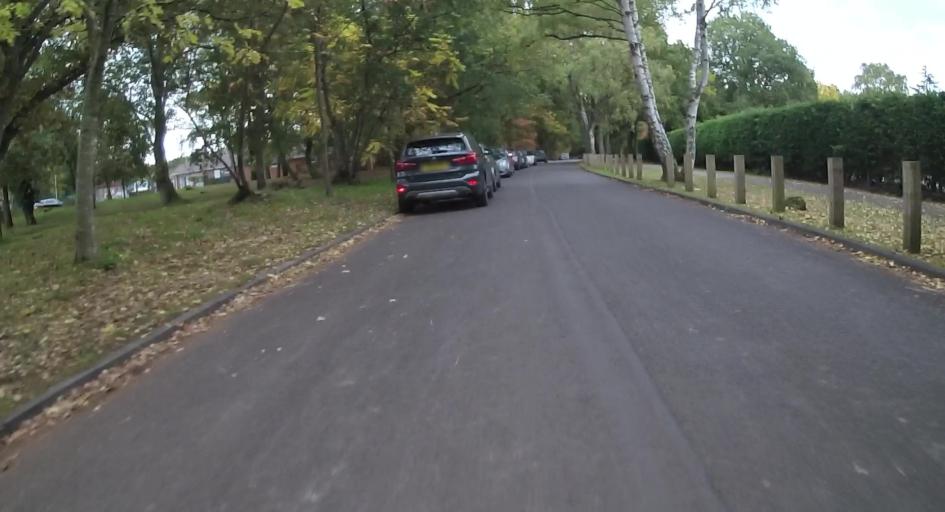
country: GB
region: England
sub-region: Bracknell Forest
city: Crowthorne
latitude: 51.3910
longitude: -0.7790
